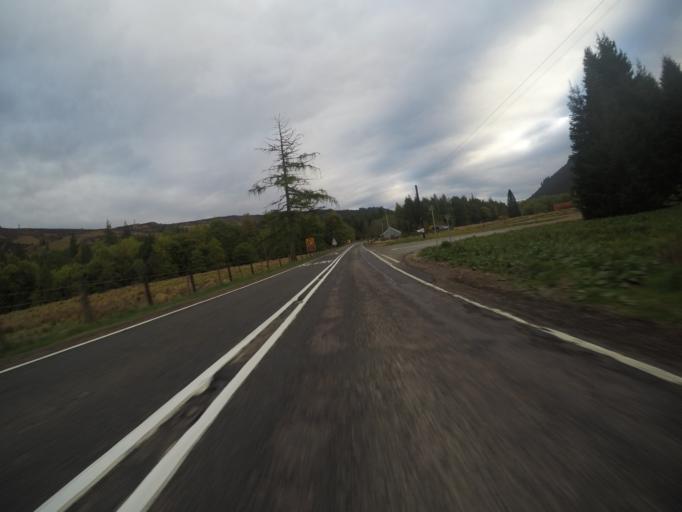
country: GB
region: Scotland
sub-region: Highland
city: Spean Bridge
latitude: 57.0355
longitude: -4.8123
